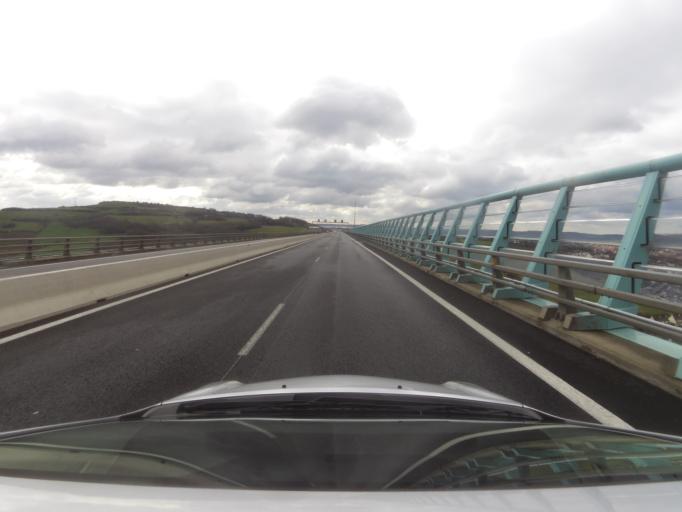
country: FR
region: Nord-Pas-de-Calais
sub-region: Departement du Pas-de-Calais
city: Saint-Leonard
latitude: 50.6985
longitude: 1.6344
